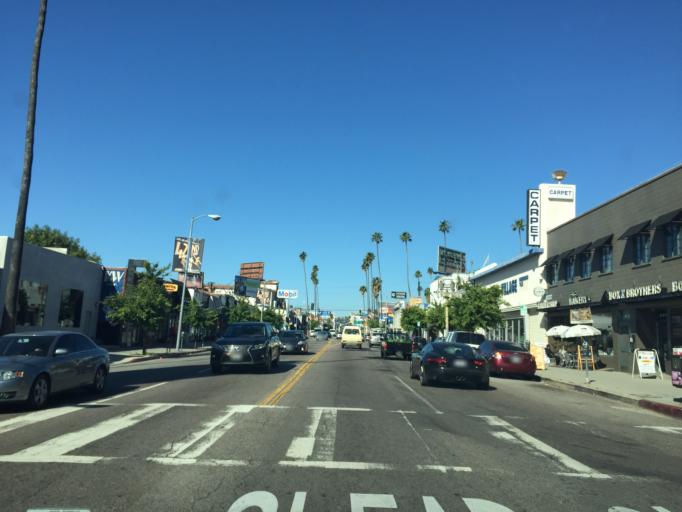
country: US
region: California
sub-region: Los Angeles County
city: Hollywood
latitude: 34.1018
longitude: -118.3122
